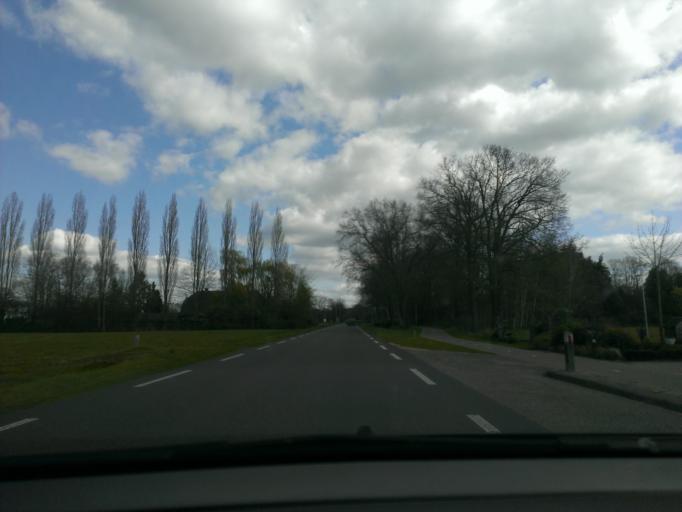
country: NL
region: Overijssel
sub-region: Gemeente Borne
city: Borne
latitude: 52.3098
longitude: 6.7091
